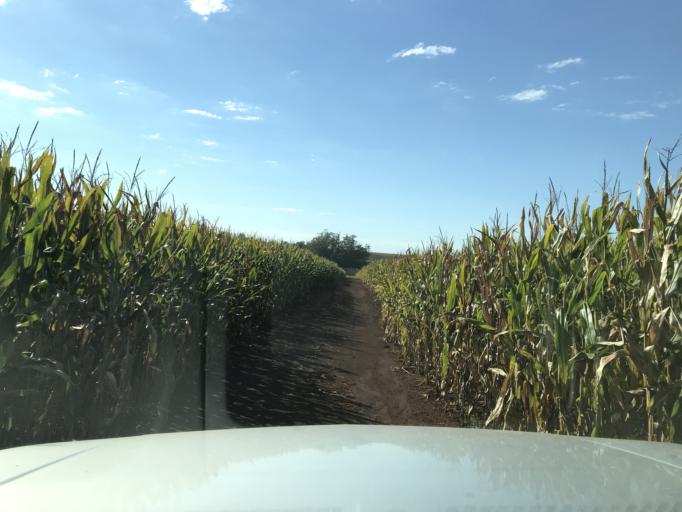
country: BR
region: Parana
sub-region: Palotina
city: Palotina
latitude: -24.2639
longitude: -53.8086
